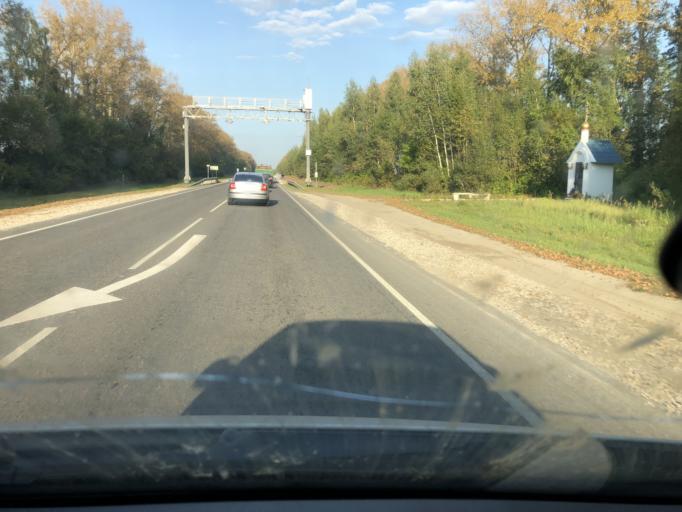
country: RU
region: Kaluga
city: Peremyshl'
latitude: 54.2492
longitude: 36.1035
